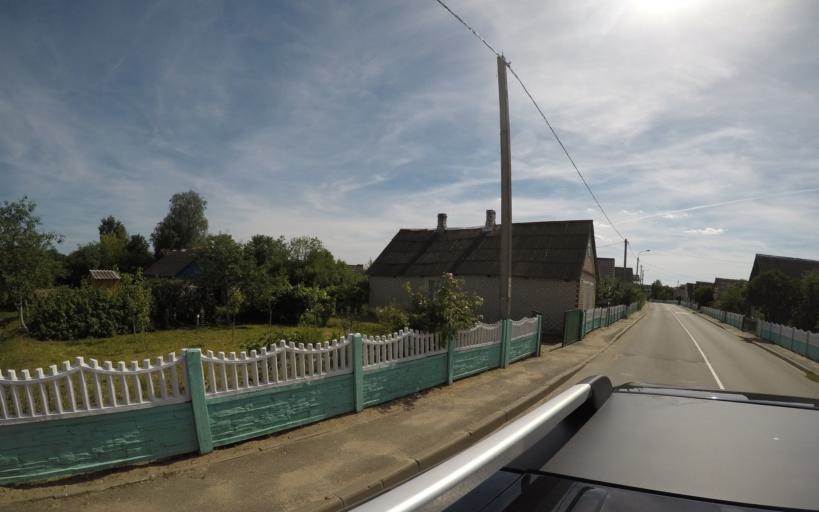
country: BY
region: Grodnenskaya
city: Hal'shany
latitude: 54.2598
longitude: 26.0161
